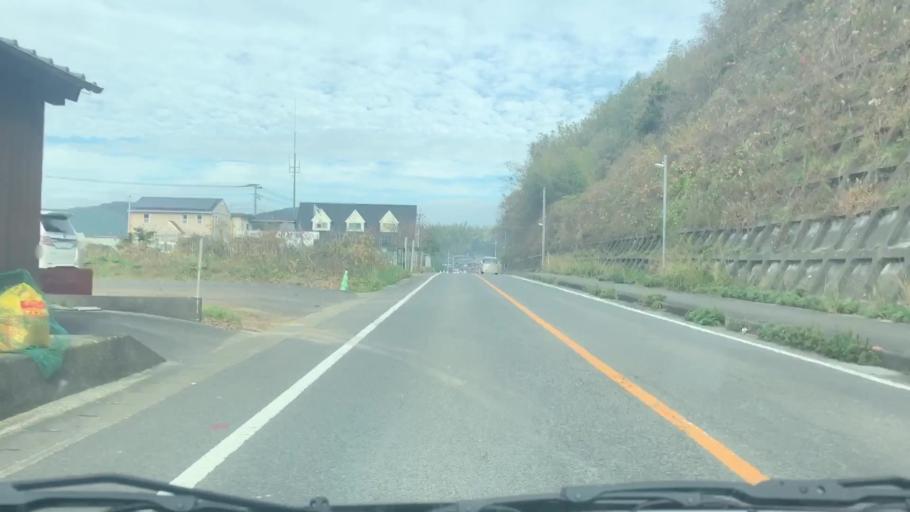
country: JP
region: Saga Prefecture
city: Karatsu
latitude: 33.3922
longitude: 129.9869
